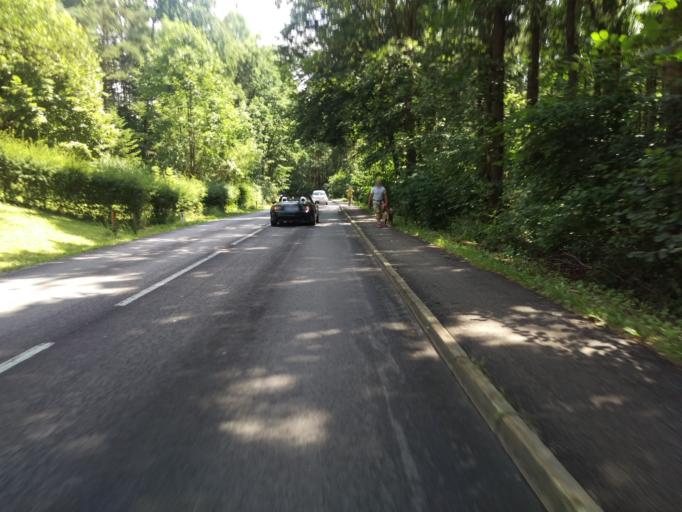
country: AT
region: Styria
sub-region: Politischer Bezirk Graz-Umgebung
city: Sankt Radegund bei Graz
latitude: 47.1403
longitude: 15.4916
